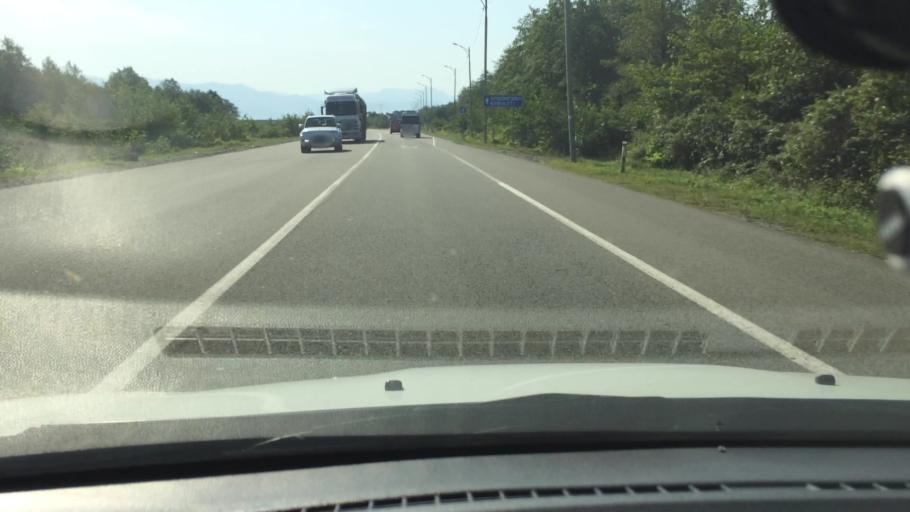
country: GE
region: Guria
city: Urek'i
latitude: 41.9259
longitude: 41.7733
